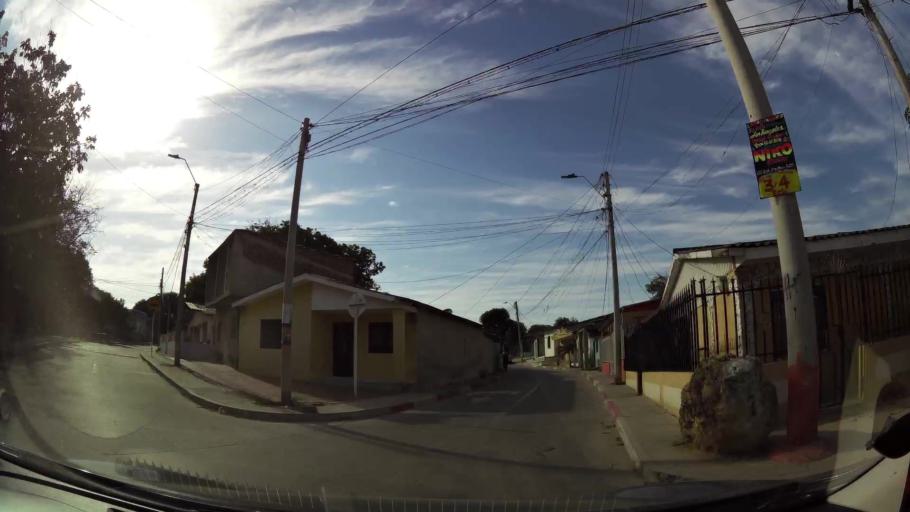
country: CO
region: Atlantico
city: Soledad
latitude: 10.9262
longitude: -74.8127
